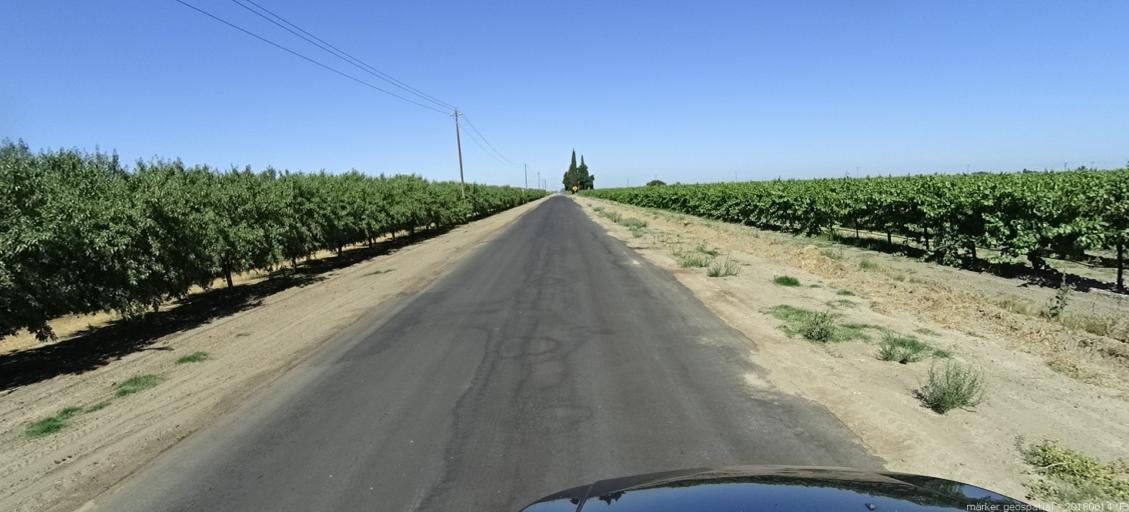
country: US
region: California
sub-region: Madera County
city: Fairmead
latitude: 36.9674
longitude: -120.1801
